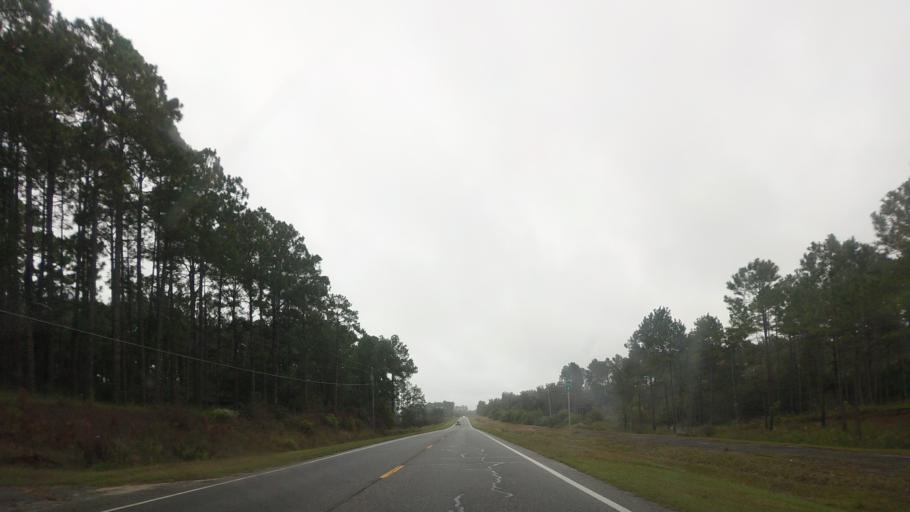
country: US
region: Georgia
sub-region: Ben Hill County
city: Fitzgerald
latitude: 31.7599
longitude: -83.2456
